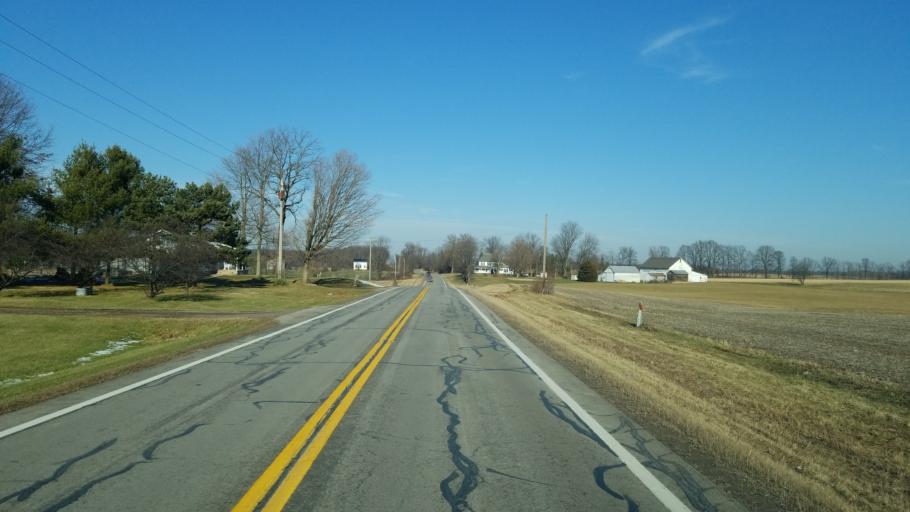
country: US
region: Ohio
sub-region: Huron County
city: Willard
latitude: 41.1334
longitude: -82.6585
